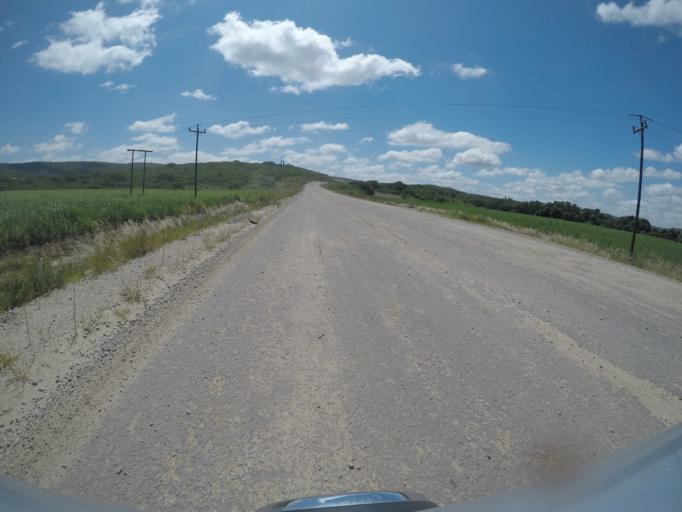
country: ZA
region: KwaZulu-Natal
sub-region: uThungulu District Municipality
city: Empangeni
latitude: -28.6434
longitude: 31.7657
